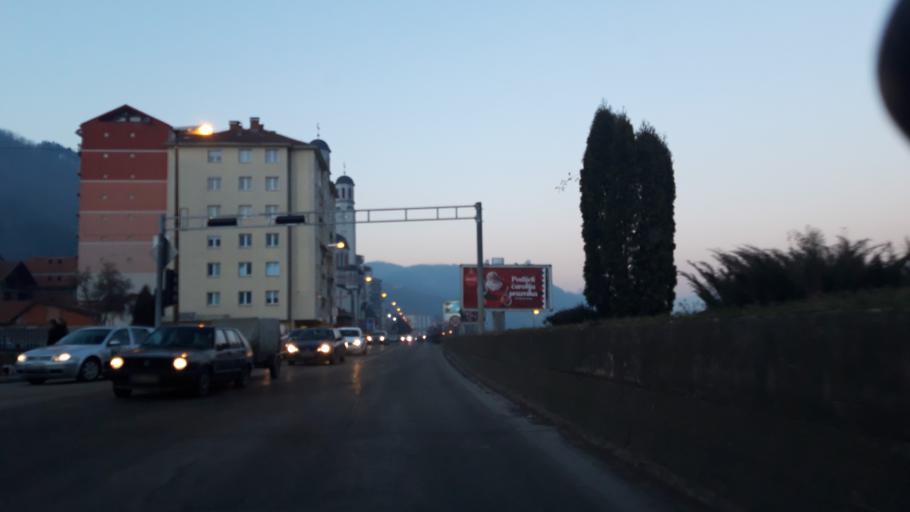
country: BA
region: Republika Srpska
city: Zvornik
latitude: 44.3865
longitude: 19.1052
